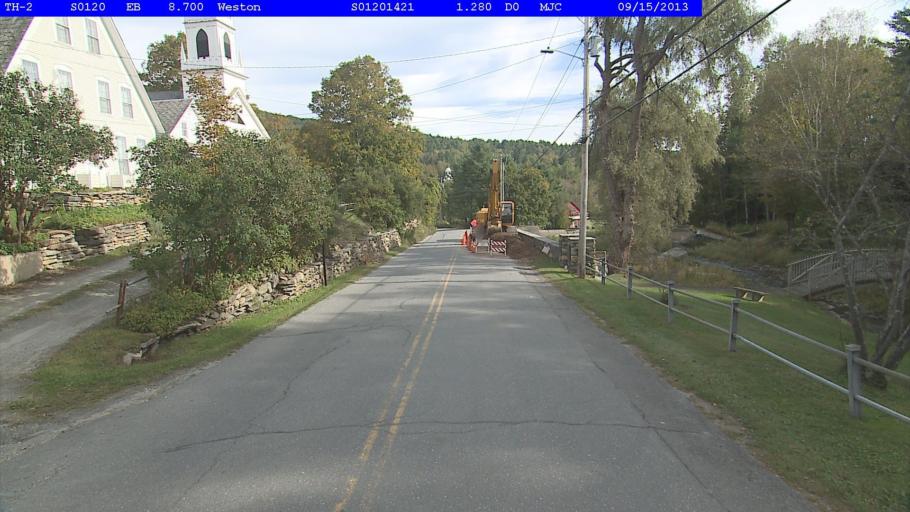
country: US
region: Vermont
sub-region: Windsor County
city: Chester
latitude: 43.2925
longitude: -72.7962
